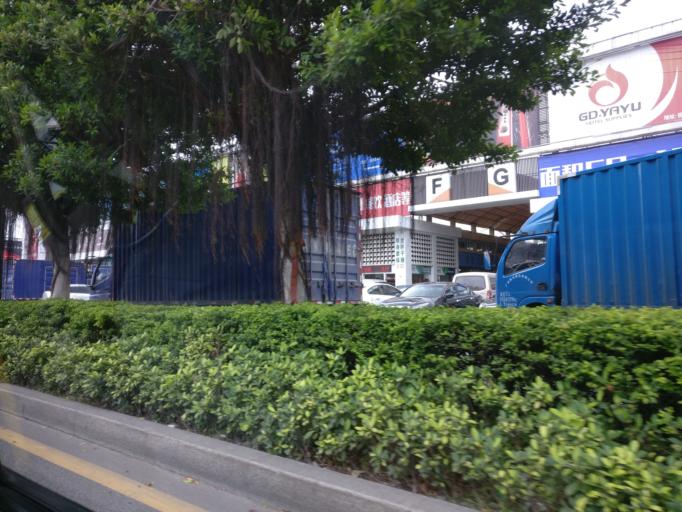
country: CN
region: Guangdong
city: Dashi
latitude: 23.0374
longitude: 113.3312
